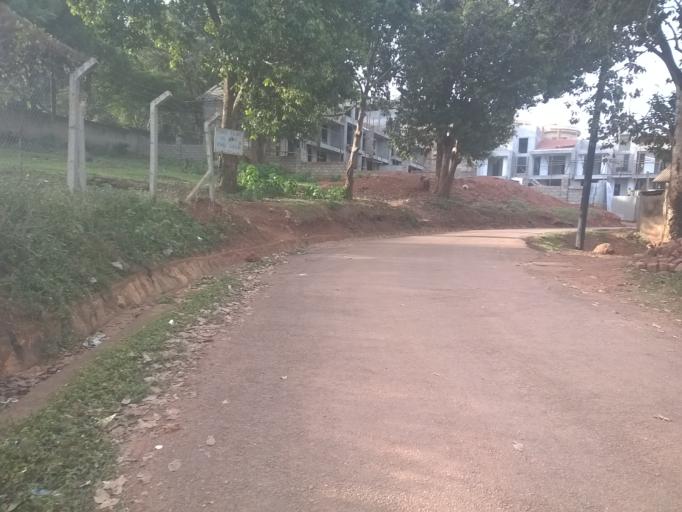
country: UG
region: Central Region
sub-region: Wakiso District
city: Kireka
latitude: 0.3244
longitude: 32.6337
